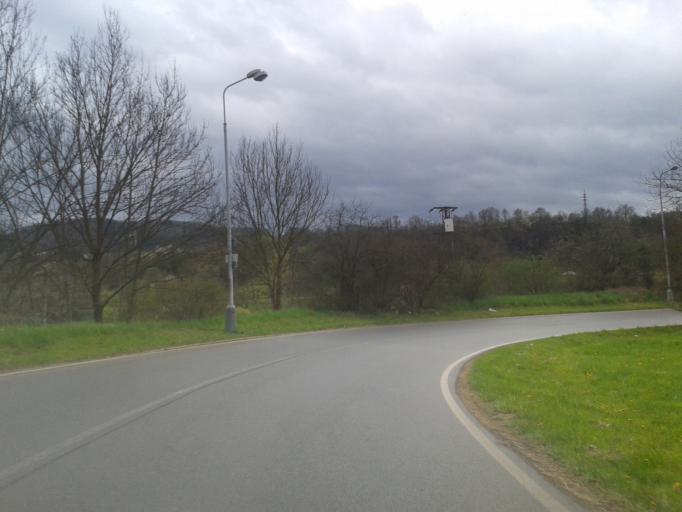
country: CZ
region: Central Bohemia
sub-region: Okres Beroun
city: Beroun
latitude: 49.9610
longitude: 14.0884
